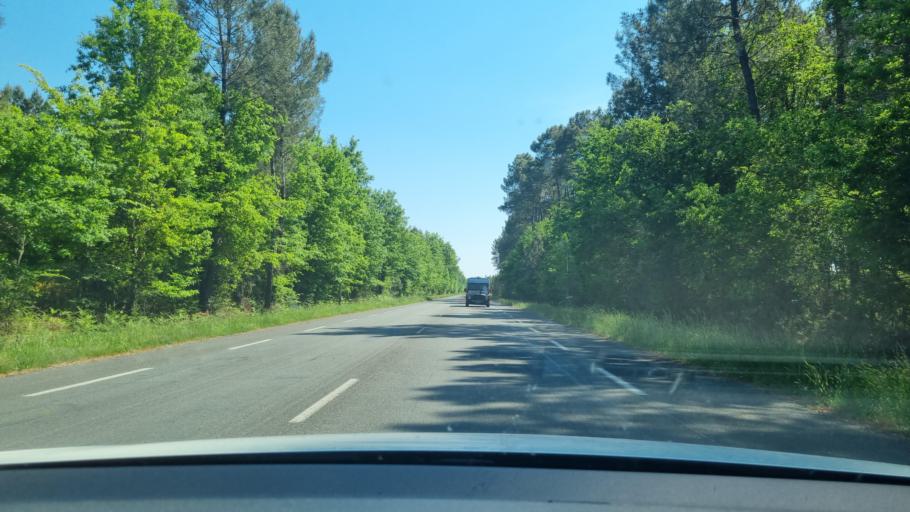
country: FR
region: Aquitaine
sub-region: Departement de la Gironde
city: Prechac
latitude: 44.2534
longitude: -0.2612
